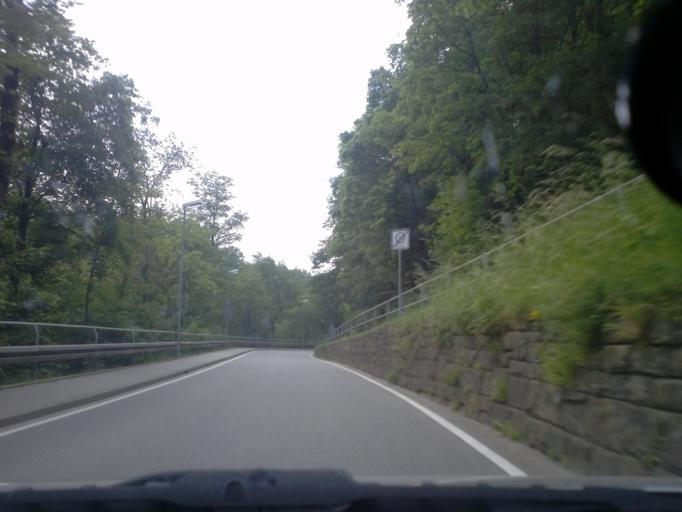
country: DE
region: Baden-Wuerttemberg
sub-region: Karlsruhe Region
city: Maulbronn
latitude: 49.0023
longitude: 8.8154
